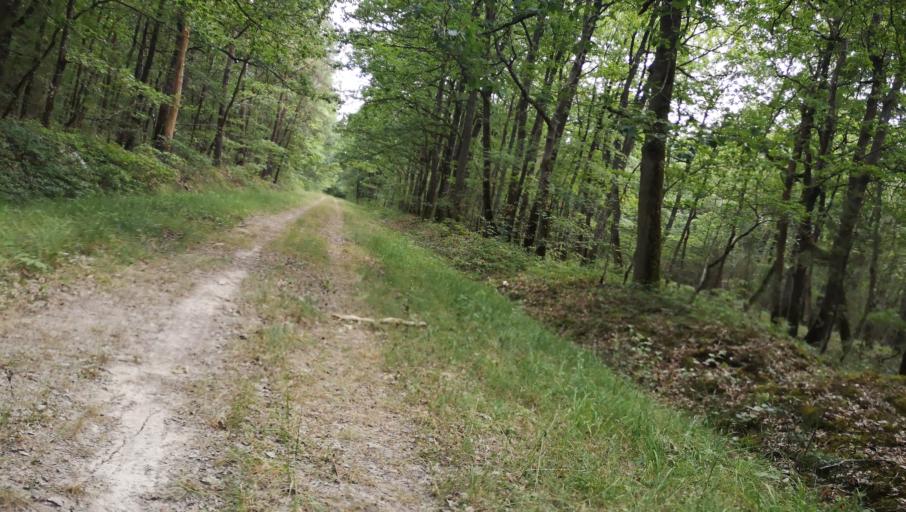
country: FR
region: Centre
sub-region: Departement du Loiret
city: Semoy
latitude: 47.9533
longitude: 1.9446
